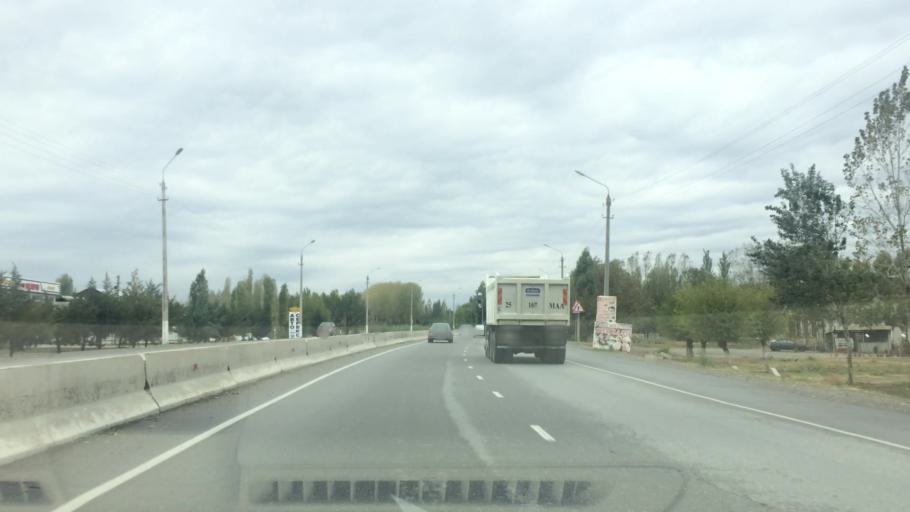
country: UZ
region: Jizzax
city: Jizzax
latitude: 39.9914
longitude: 67.5837
